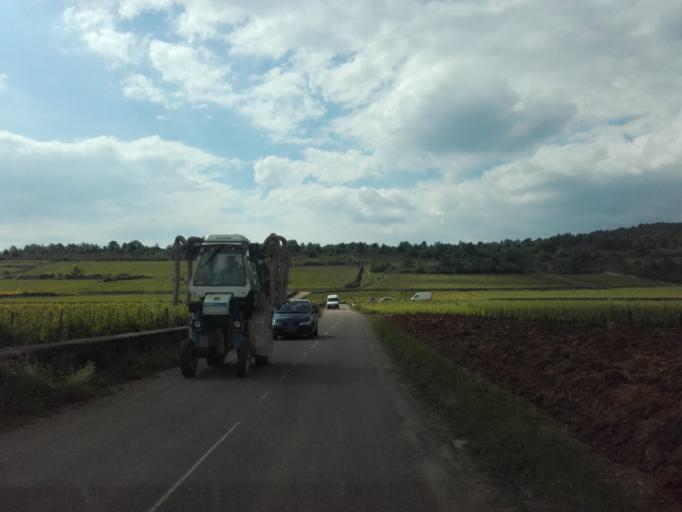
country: FR
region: Bourgogne
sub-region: Departement de la Cote-d'Or
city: Corpeau
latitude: 46.9467
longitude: 4.7427
